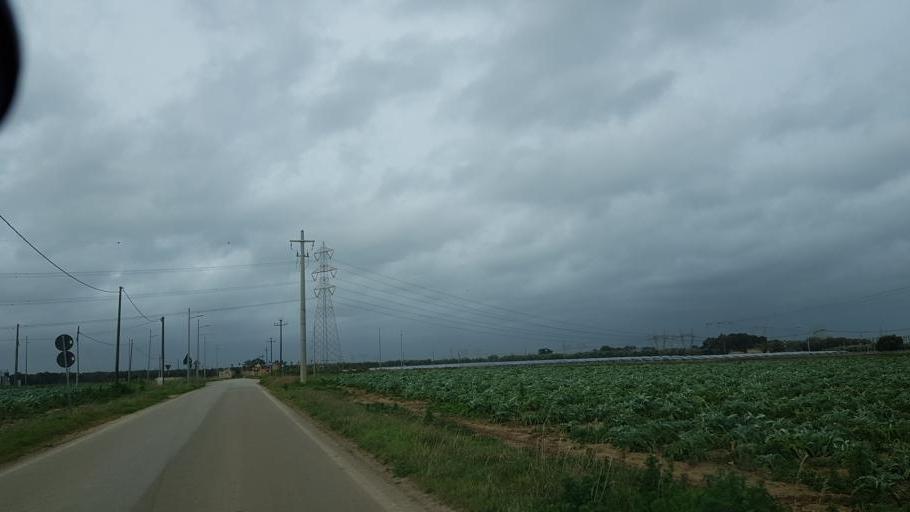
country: IT
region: Apulia
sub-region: Provincia di Brindisi
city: La Rosa
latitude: 40.5942
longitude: 17.9055
